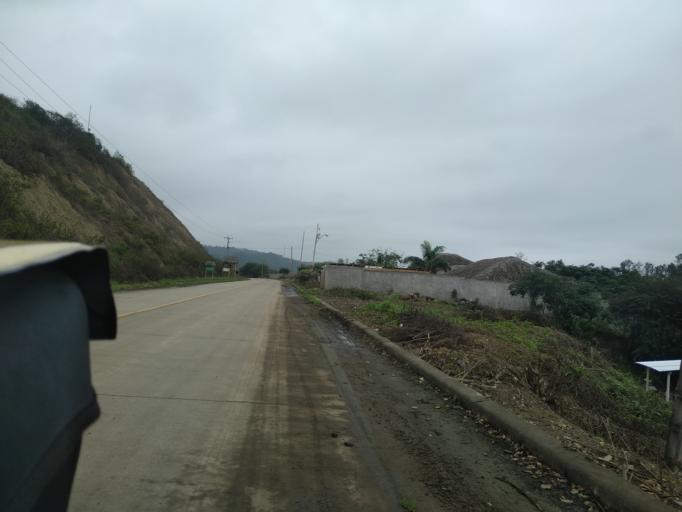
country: EC
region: Manabi
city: Jipijapa
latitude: -1.6543
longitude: -80.8208
